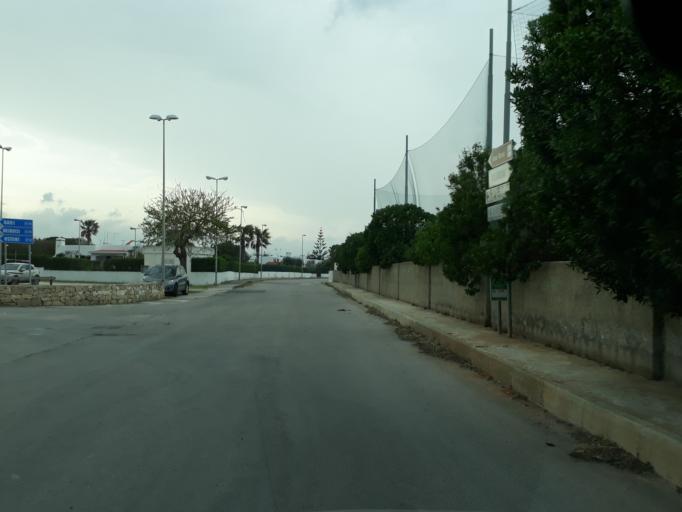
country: IT
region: Apulia
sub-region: Provincia di Brindisi
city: Ostuni
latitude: 40.7907
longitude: 17.5826
